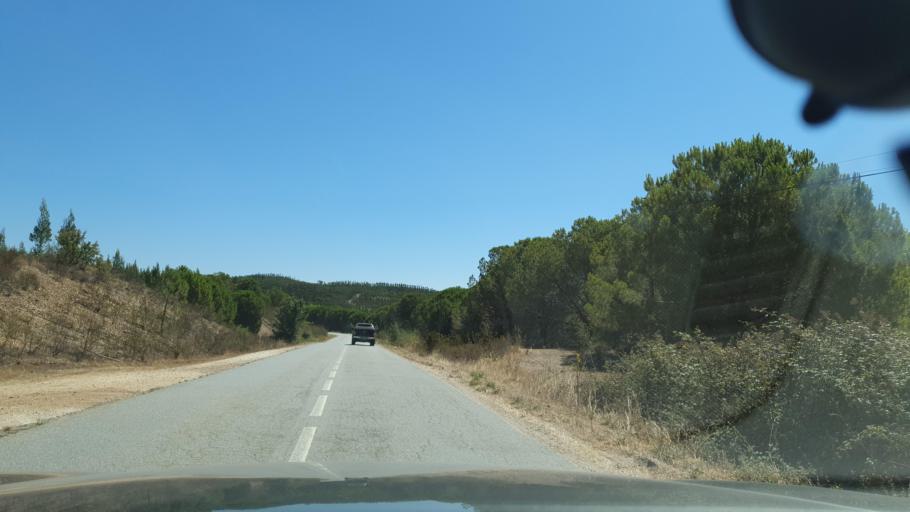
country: PT
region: Faro
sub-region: Monchique
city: Monchique
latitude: 37.4246
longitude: -8.5363
